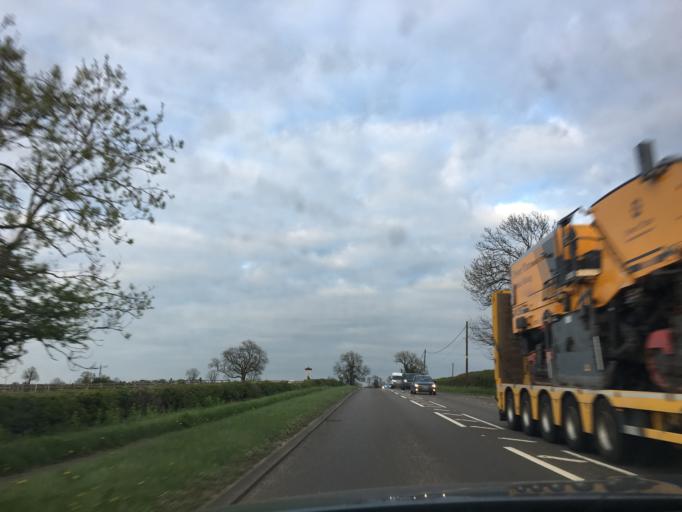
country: GB
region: England
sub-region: Leicestershire
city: Houghton on the Hill
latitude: 52.6291
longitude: -1.0138
